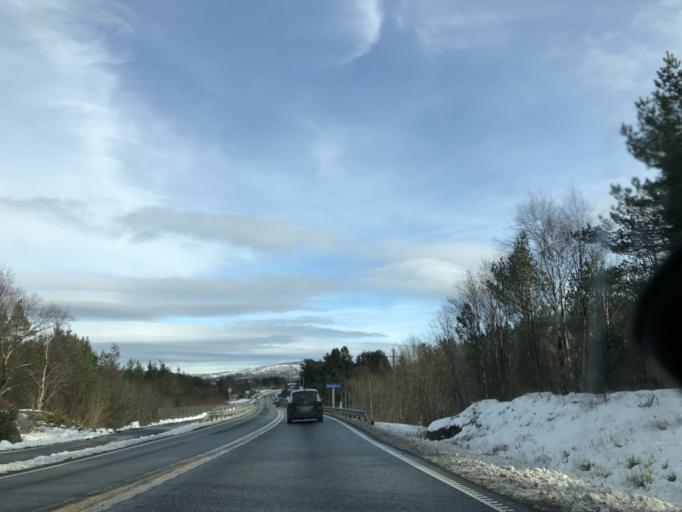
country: NO
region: Rogaland
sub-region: Tysvaer
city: Tysvaer
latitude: 59.3154
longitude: 5.4501
